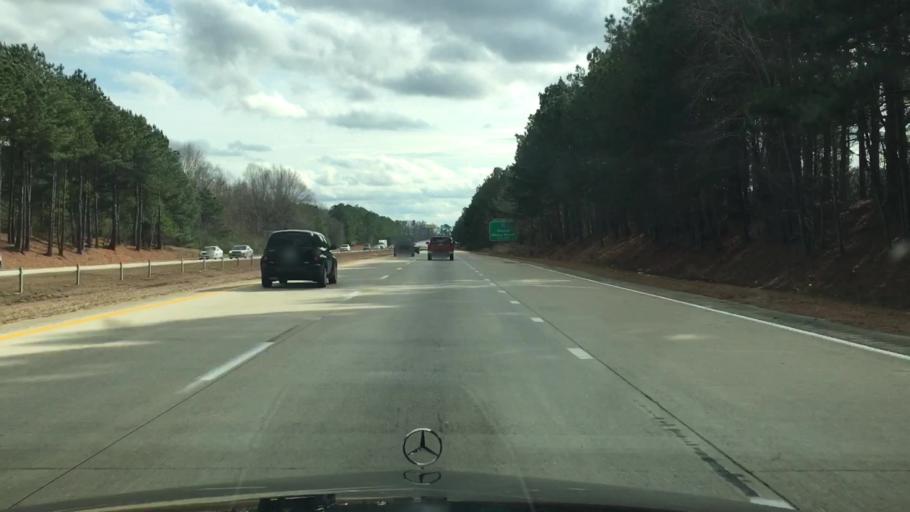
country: US
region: North Carolina
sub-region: Johnston County
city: Benson
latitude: 35.4188
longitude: -78.5283
